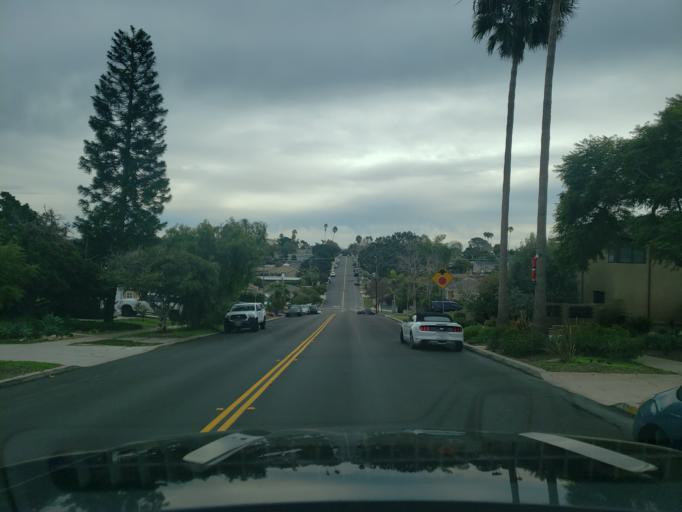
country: US
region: California
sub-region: San Diego County
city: Coronado
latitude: 32.7349
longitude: -117.2421
